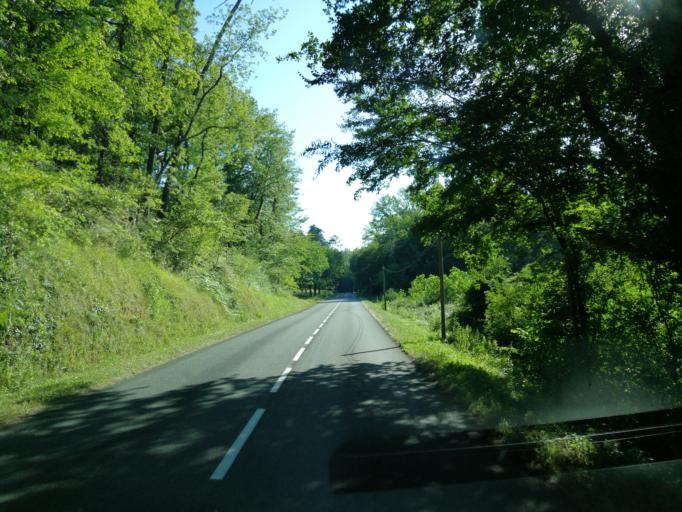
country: FR
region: Midi-Pyrenees
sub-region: Departement du Lot
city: Prayssac
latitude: 44.5945
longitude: 1.1769
